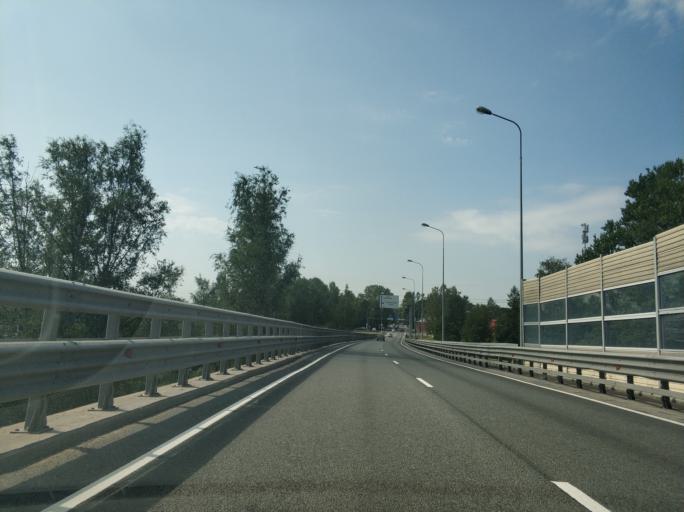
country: RU
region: St.-Petersburg
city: Krasnogvargeisky
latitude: 59.9804
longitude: 30.5056
